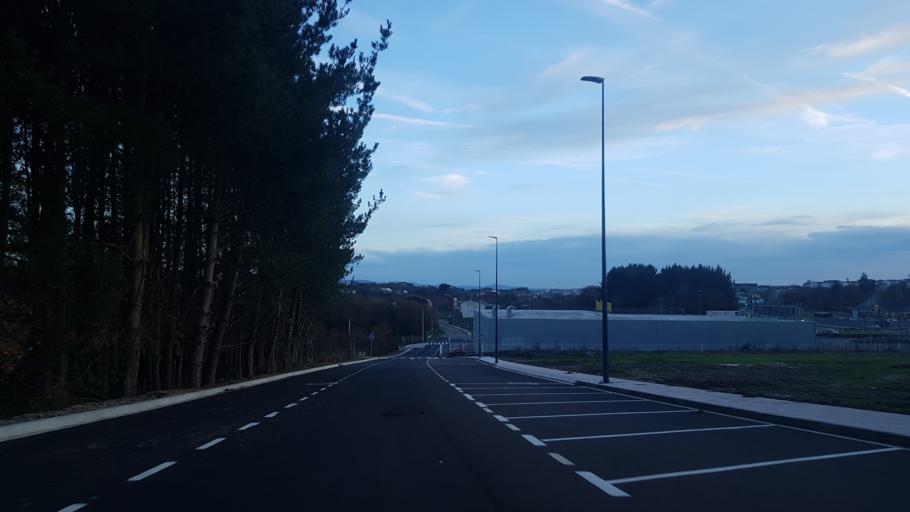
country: ES
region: Galicia
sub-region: Provincia de Lugo
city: Lugo
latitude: 43.0390
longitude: -7.5658
